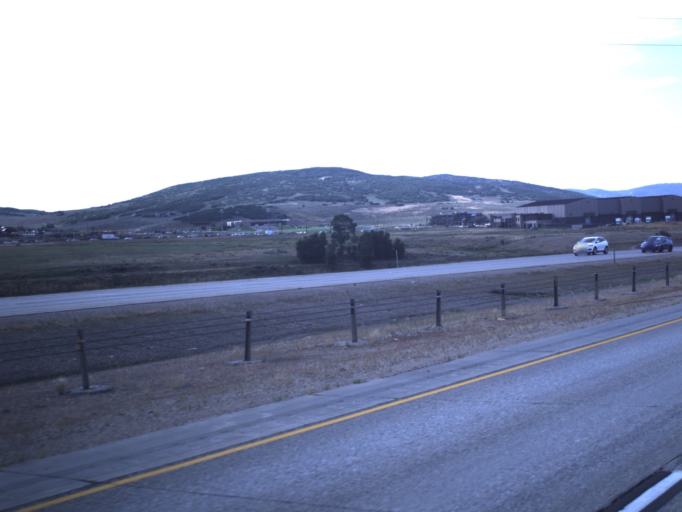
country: US
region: Utah
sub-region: Summit County
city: Park City
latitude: 40.6758
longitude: -111.4606
